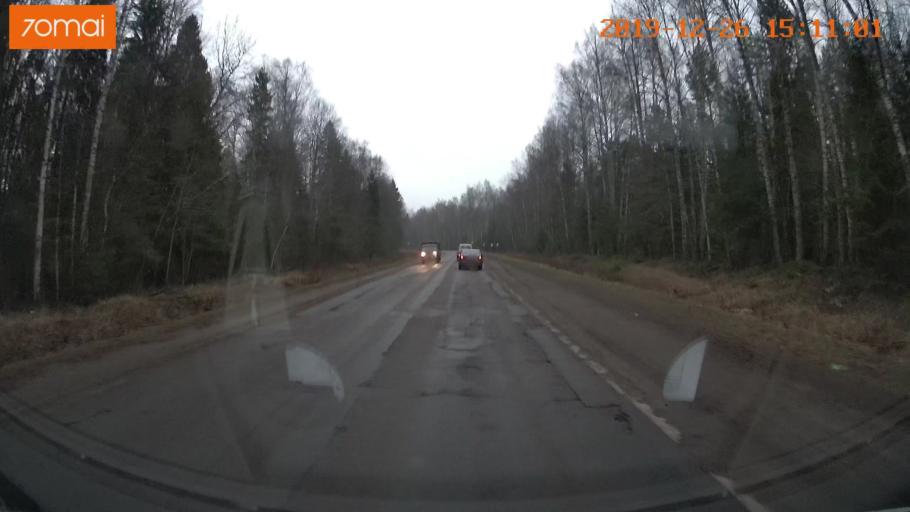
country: RU
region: Jaroslavl
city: Rybinsk
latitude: 58.1366
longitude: 38.8567
